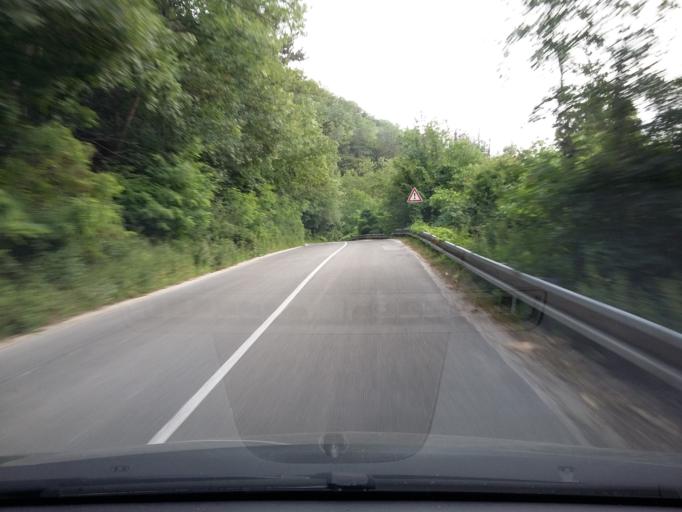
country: SK
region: Trnavsky
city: Smolenice
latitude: 48.5451
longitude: 17.4229
